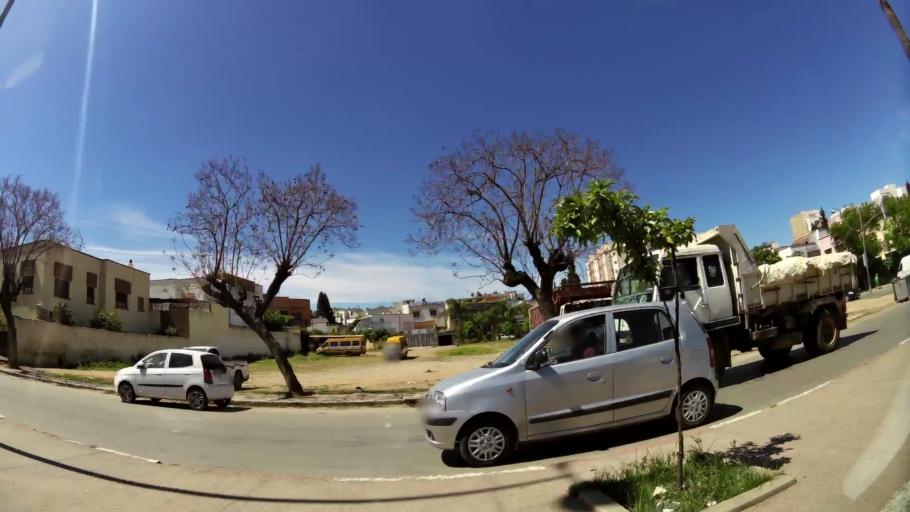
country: MA
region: Meknes-Tafilalet
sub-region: Meknes
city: Meknes
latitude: 33.9058
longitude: -5.5286
